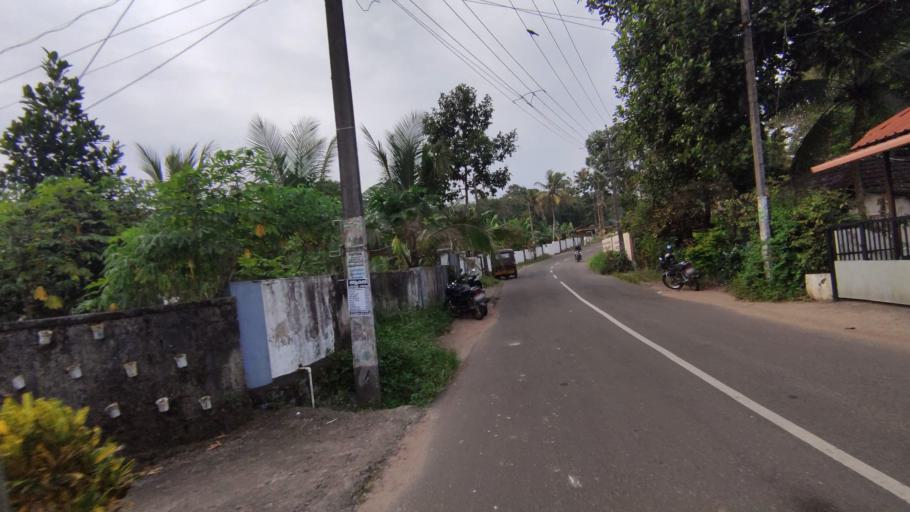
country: IN
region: Kerala
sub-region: Kottayam
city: Kottayam
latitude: 9.6410
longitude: 76.5176
